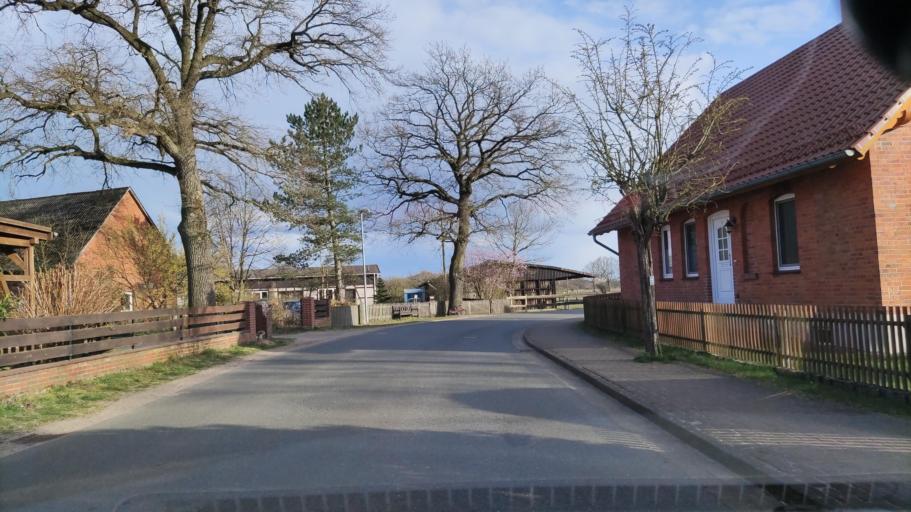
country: DE
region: Lower Saxony
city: Klein Gusborn
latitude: 53.0785
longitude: 11.2170
